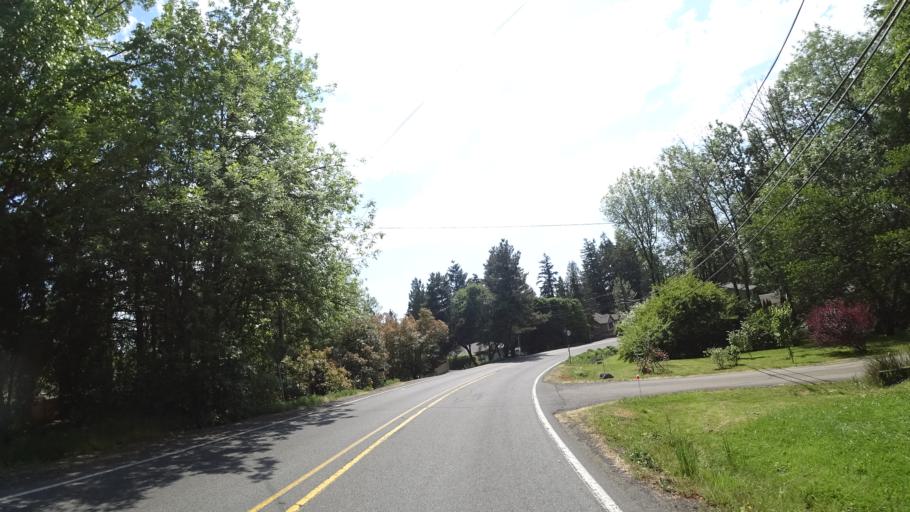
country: US
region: Oregon
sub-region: Washington County
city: Metzger
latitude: 45.4541
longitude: -122.7499
